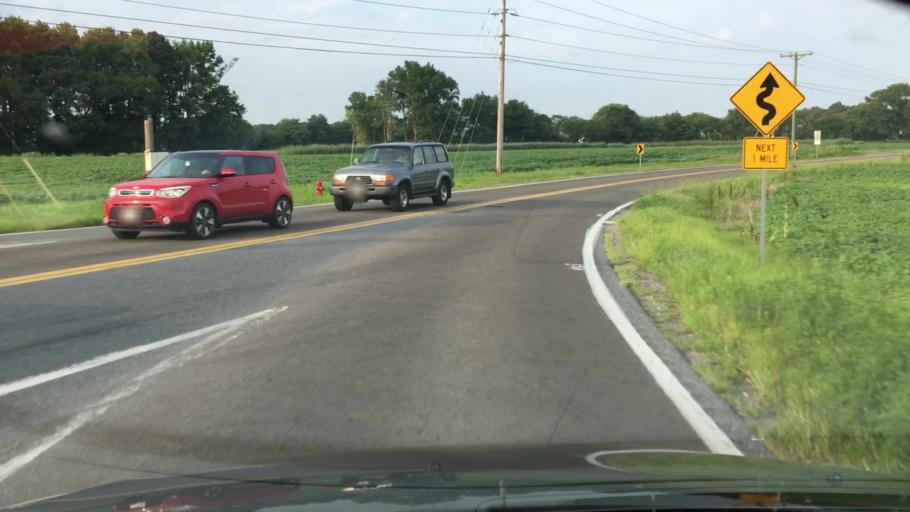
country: US
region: Delaware
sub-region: Sussex County
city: Ocean View
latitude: 38.5045
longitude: -75.1261
